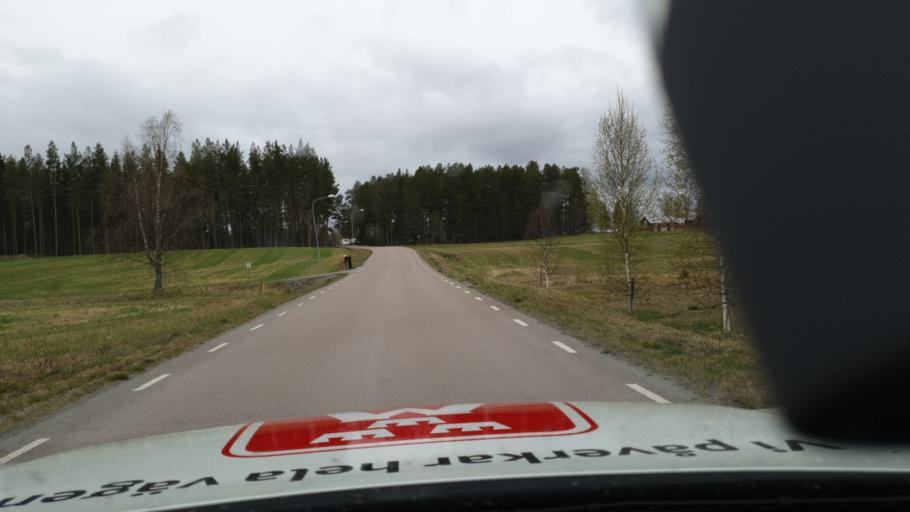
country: SE
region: Jaemtland
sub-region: OEstersunds Kommun
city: Lit
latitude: 63.2954
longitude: 14.9796
